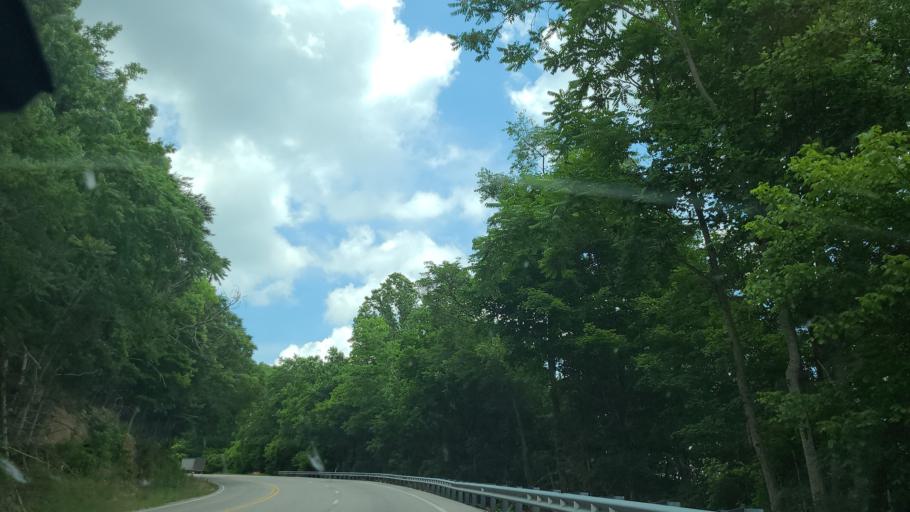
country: US
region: Tennessee
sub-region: Cumberland County
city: Lake Tansi
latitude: 35.7719
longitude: -85.0409
